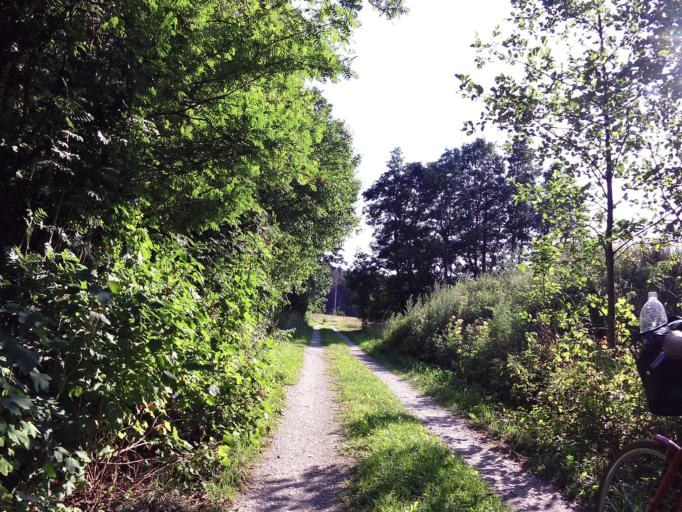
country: EE
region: Hiiumaa
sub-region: Kaerdla linn
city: Kardla
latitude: 58.8869
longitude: 22.2505
